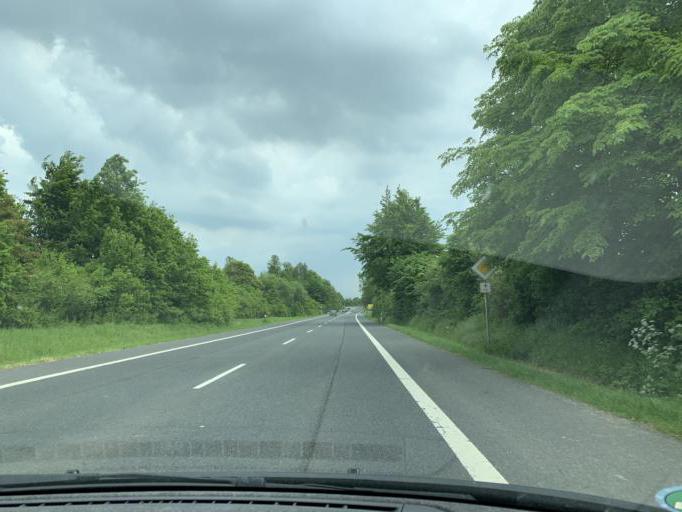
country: DE
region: North Rhine-Westphalia
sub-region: Regierungsbezirk Koln
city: Norvenich
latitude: 50.7644
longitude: 6.6339
